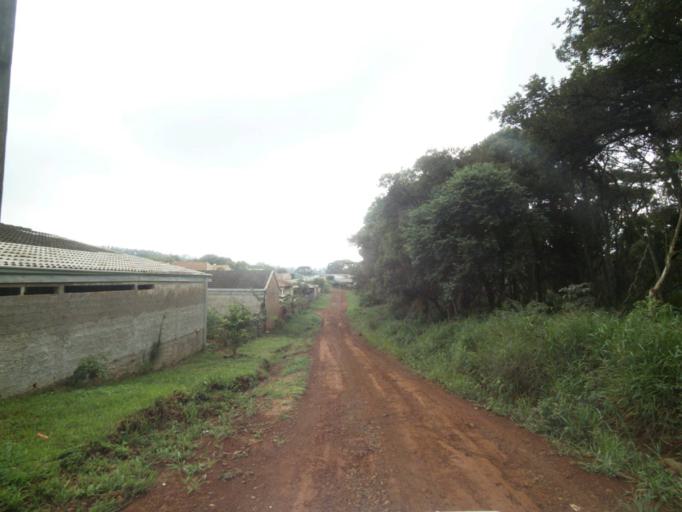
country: BR
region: Parana
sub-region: Pitanga
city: Pitanga
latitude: -24.9424
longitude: -51.8725
